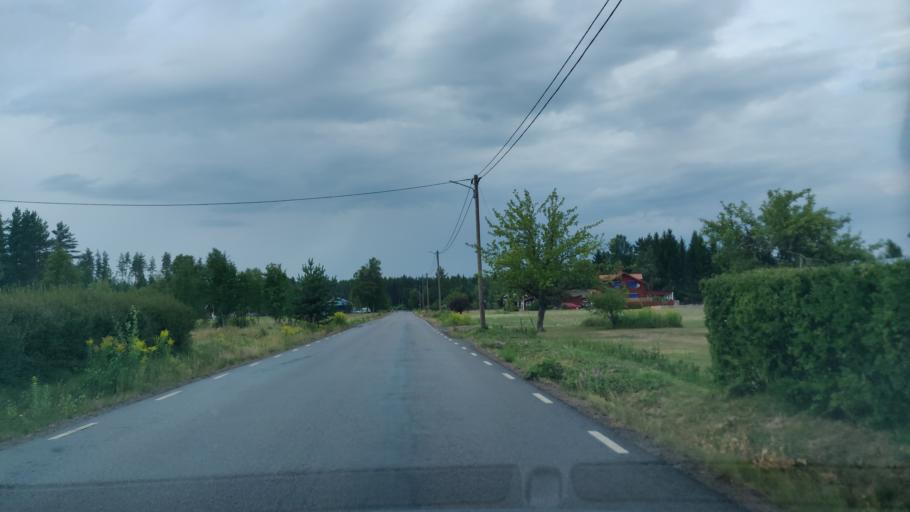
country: SE
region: Vaermland
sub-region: Munkfors Kommun
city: Munkfors
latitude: 59.8634
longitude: 13.5469
